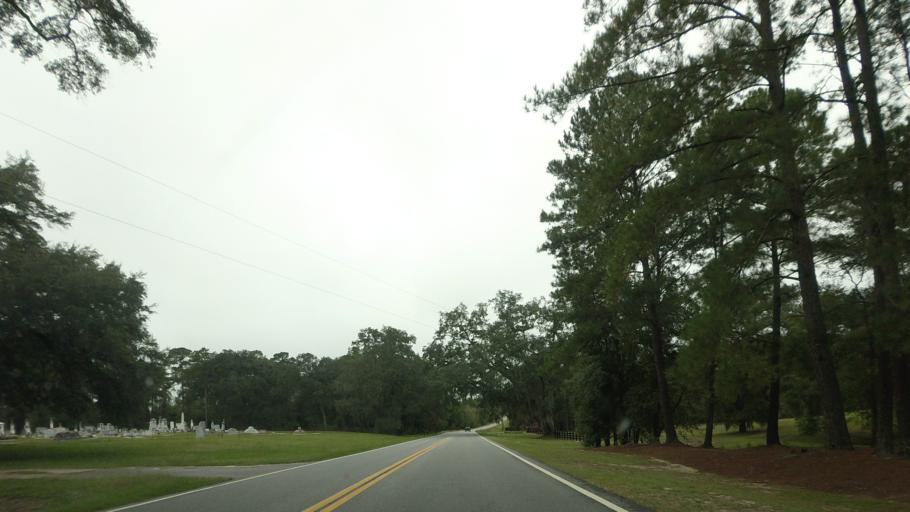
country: US
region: Georgia
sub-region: Berrien County
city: Enigma
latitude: 31.4012
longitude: -83.2400
